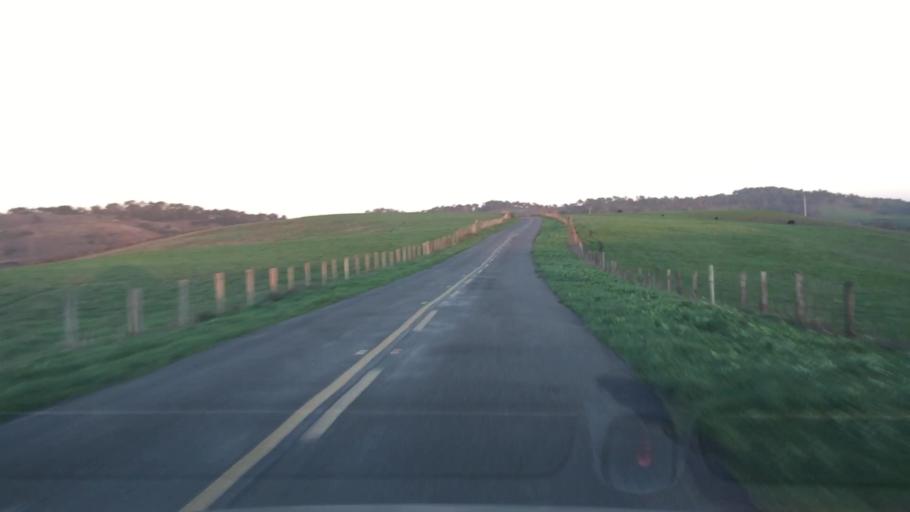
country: US
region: California
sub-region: Marin County
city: Inverness
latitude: 38.1195
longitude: -122.9186
